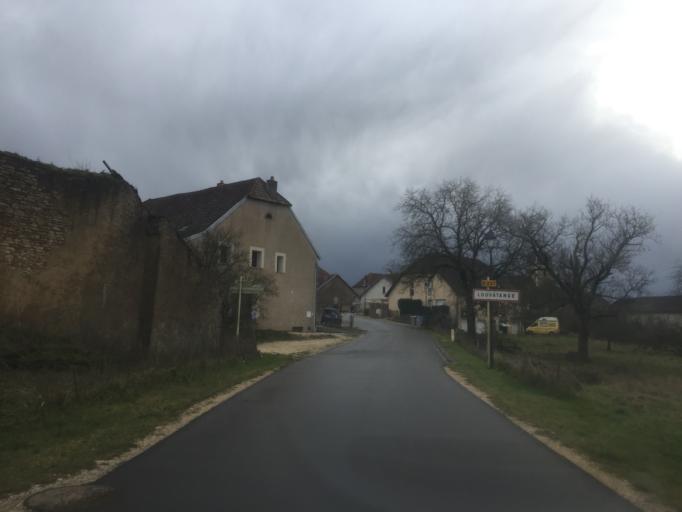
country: FR
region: Franche-Comte
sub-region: Departement du Jura
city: Dampierre
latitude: 47.1978
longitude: 5.7166
